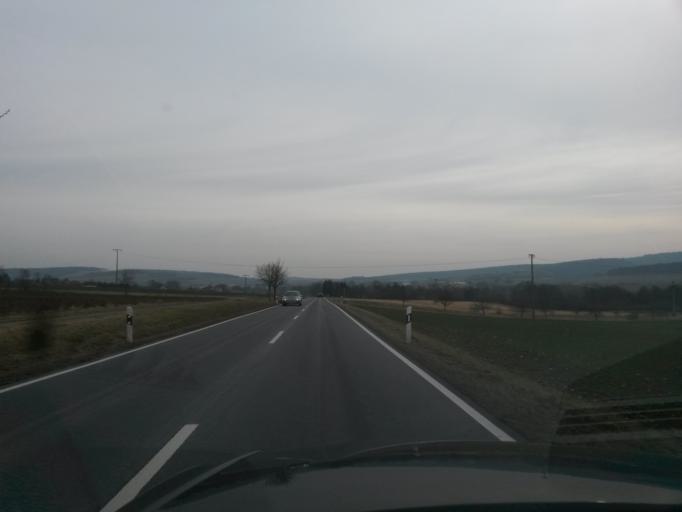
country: DE
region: Bavaria
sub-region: Regierungsbezirk Unterfranken
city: Ostheim vor der Rhon
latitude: 50.4649
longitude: 10.2112
